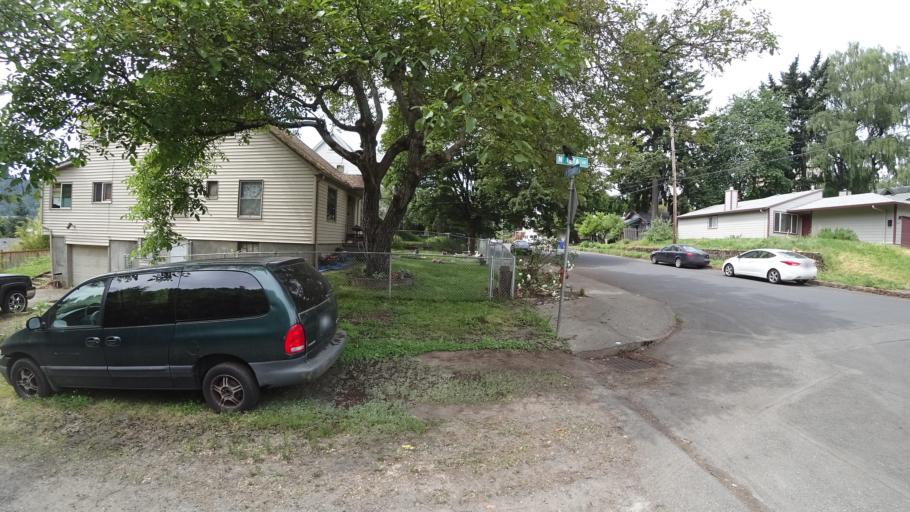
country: US
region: Oregon
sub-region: Washington County
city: West Haven
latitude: 45.5889
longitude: -122.7587
